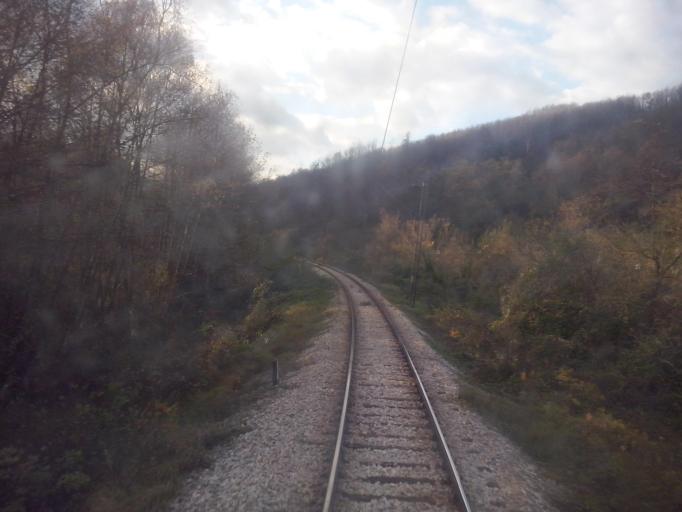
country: RS
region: Central Serbia
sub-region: Zlatiborski Okrug
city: Kosjeric
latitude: 43.9825
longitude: 19.9401
